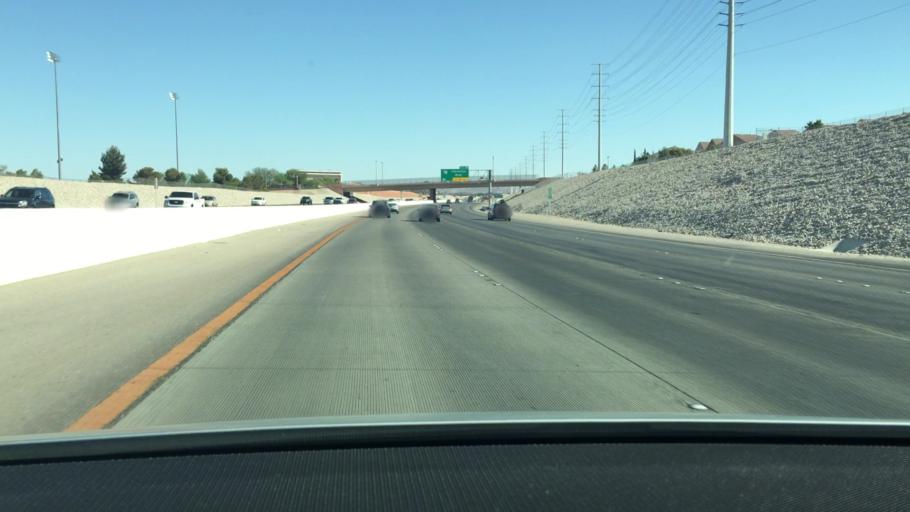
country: US
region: Nevada
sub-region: Clark County
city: Summerlin South
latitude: 36.1735
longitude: -115.3381
